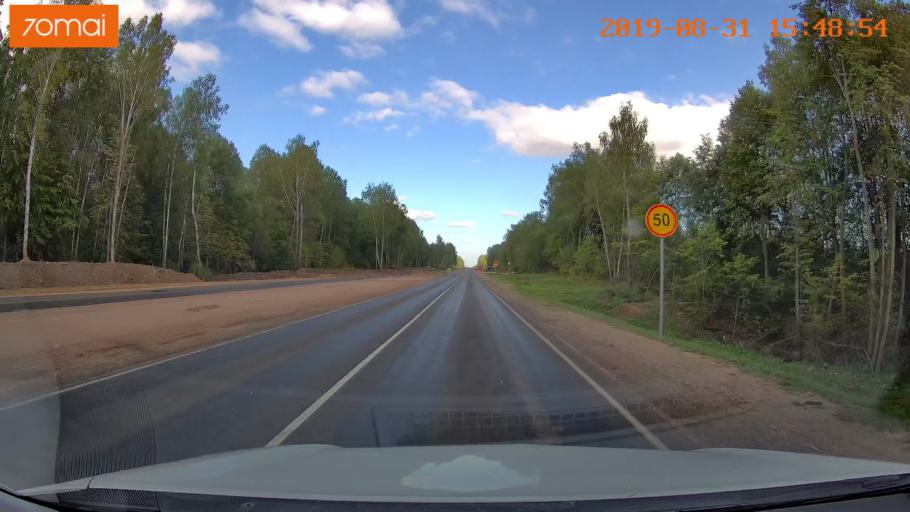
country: RU
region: Kaluga
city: Yukhnov
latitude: 54.6887
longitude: 35.0418
